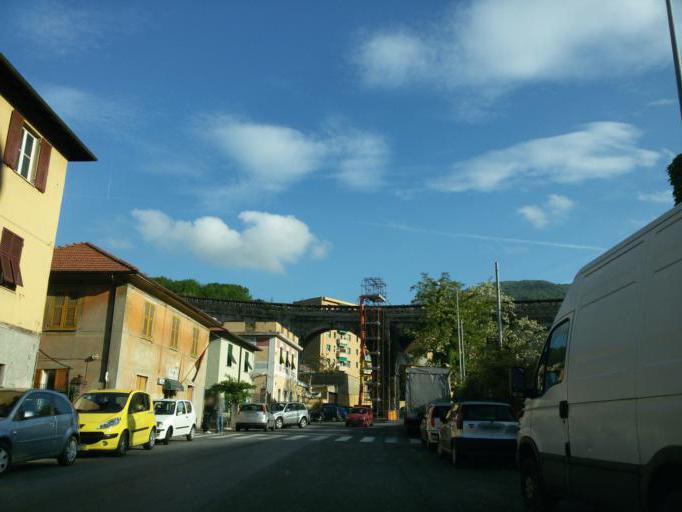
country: IT
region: Liguria
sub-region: Provincia di Genova
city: Piccarello
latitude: 44.4572
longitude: 8.9780
